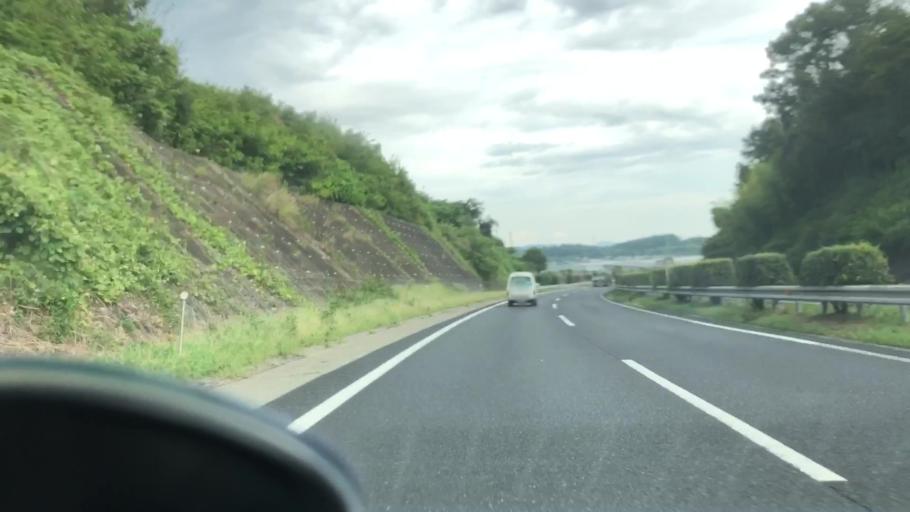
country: JP
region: Hyogo
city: Yashiro
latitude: 34.9369
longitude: 134.8538
